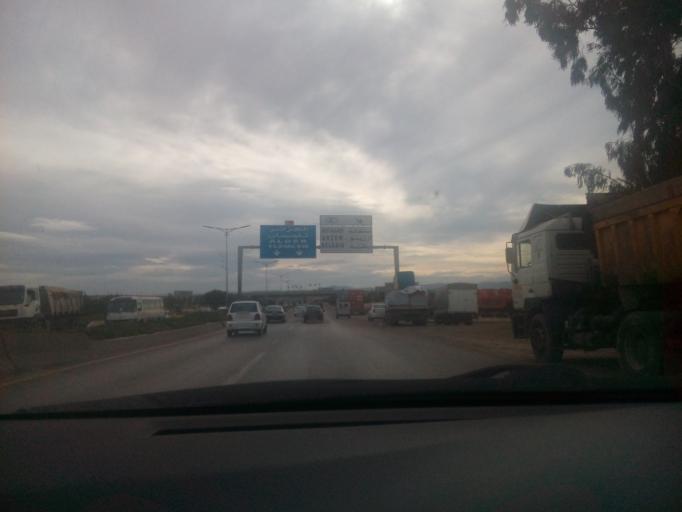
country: DZ
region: Oran
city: Es Senia
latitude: 35.6047
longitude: -0.5761
